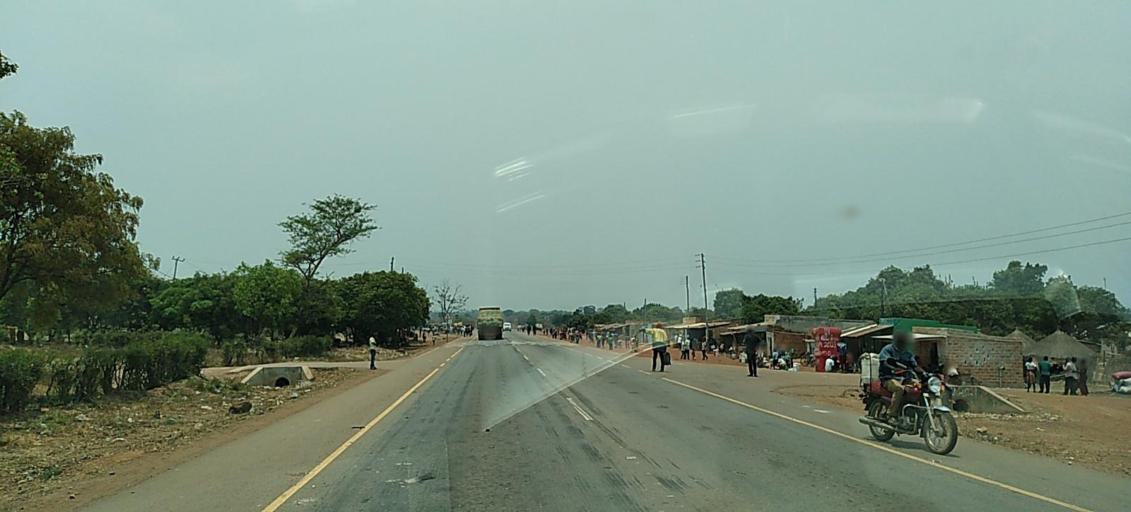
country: ZM
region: Copperbelt
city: Chililabombwe
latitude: -12.3800
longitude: 27.3198
